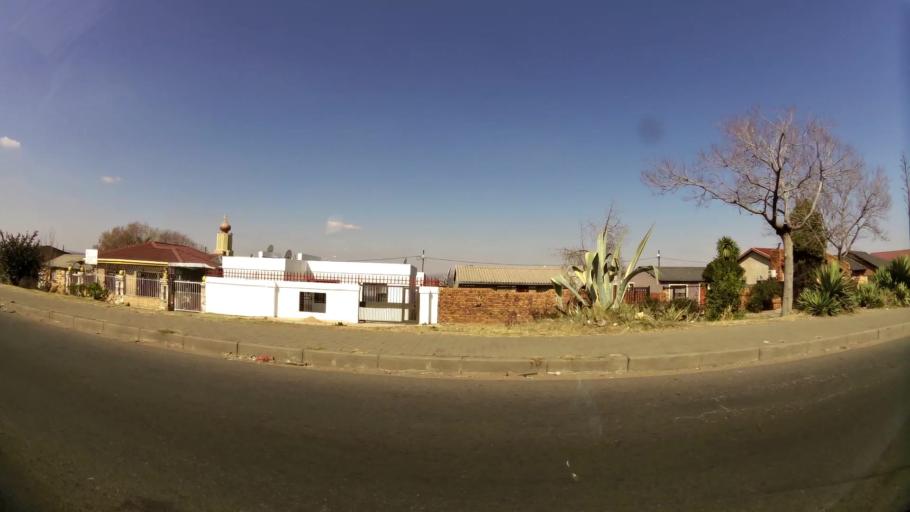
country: ZA
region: Gauteng
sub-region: City of Johannesburg Metropolitan Municipality
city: Soweto
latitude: -26.2739
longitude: 27.8721
